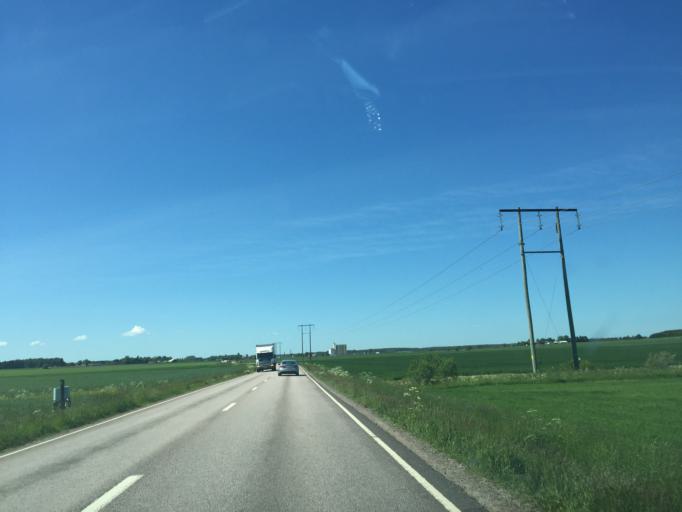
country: SE
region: OEstergoetland
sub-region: Mjolby Kommun
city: Mjolby
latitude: 58.3860
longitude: 15.1411
